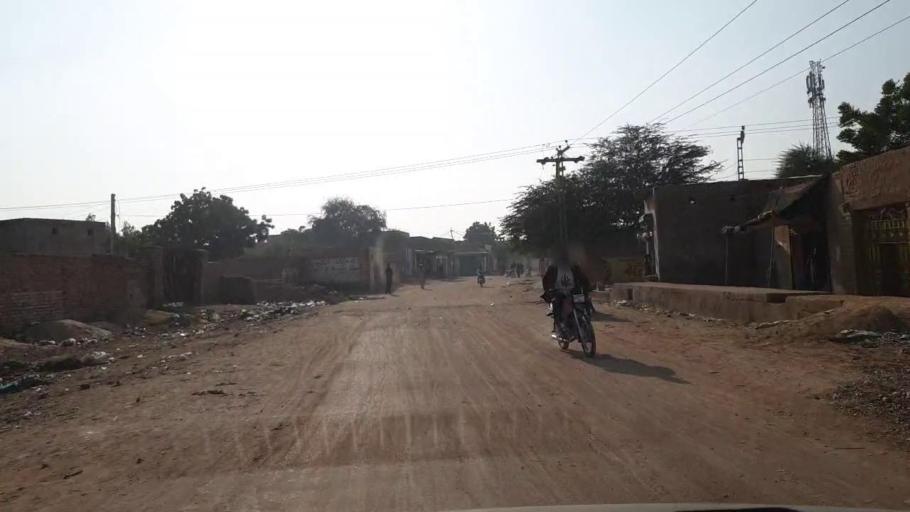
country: PK
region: Sindh
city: Kotri
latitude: 25.3530
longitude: 68.2631
